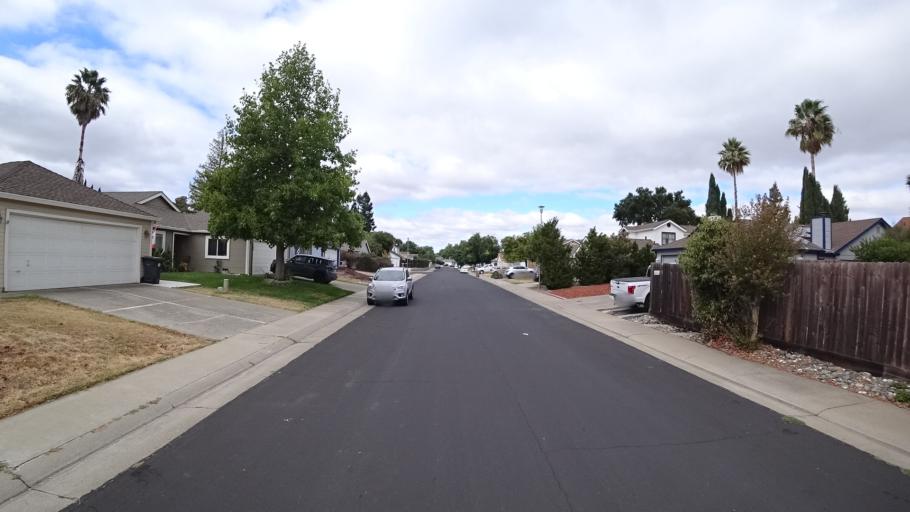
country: US
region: California
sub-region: Sacramento County
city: Laguna
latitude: 38.4133
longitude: -121.4187
